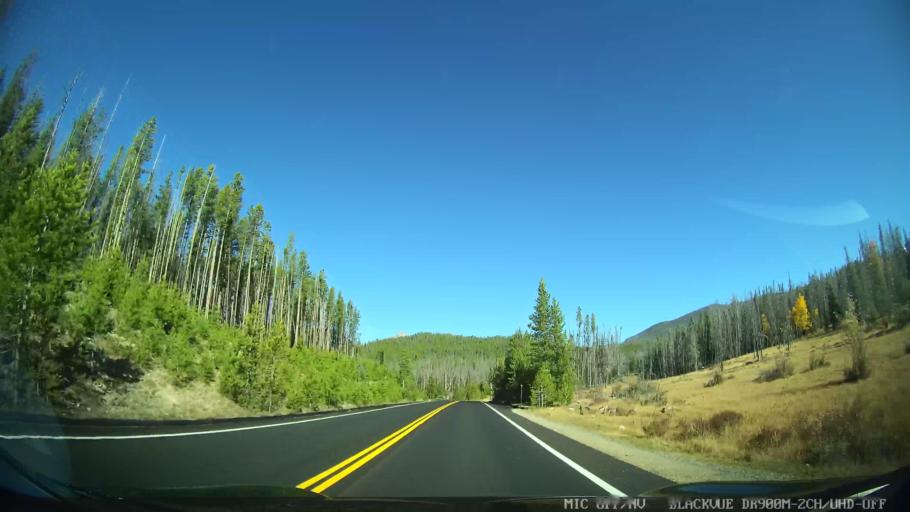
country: US
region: Colorado
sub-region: Grand County
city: Granby
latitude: 40.3163
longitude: -105.8441
